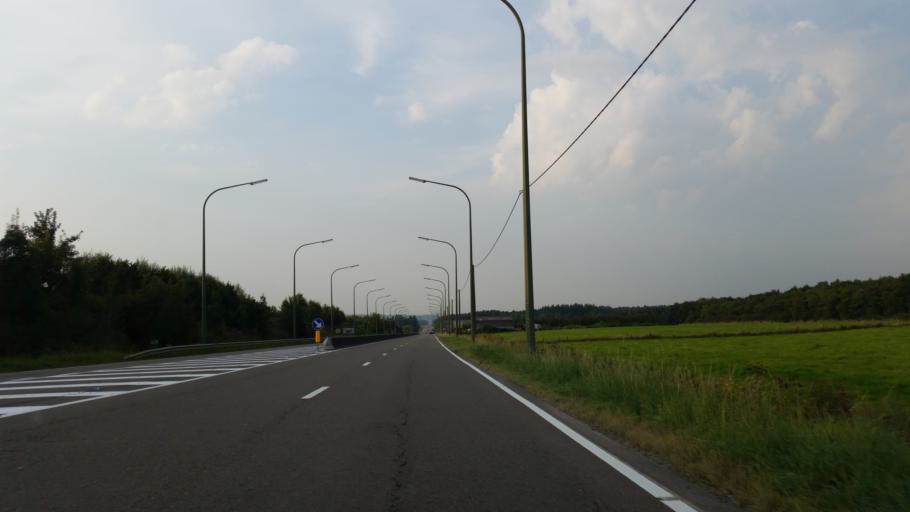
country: BE
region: Wallonia
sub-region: Province du Luxembourg
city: Marche-en-Famenne
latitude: 50.2435
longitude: 5.3453
